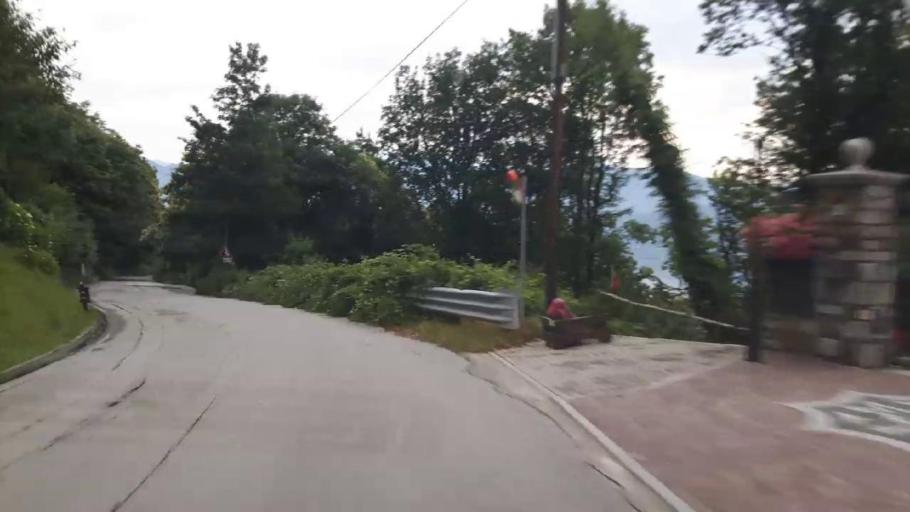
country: IT
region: Piedmont
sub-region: Provincia Verbano-Cusio-Ossola
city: Gignese
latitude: 45.8836
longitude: 8.5143
